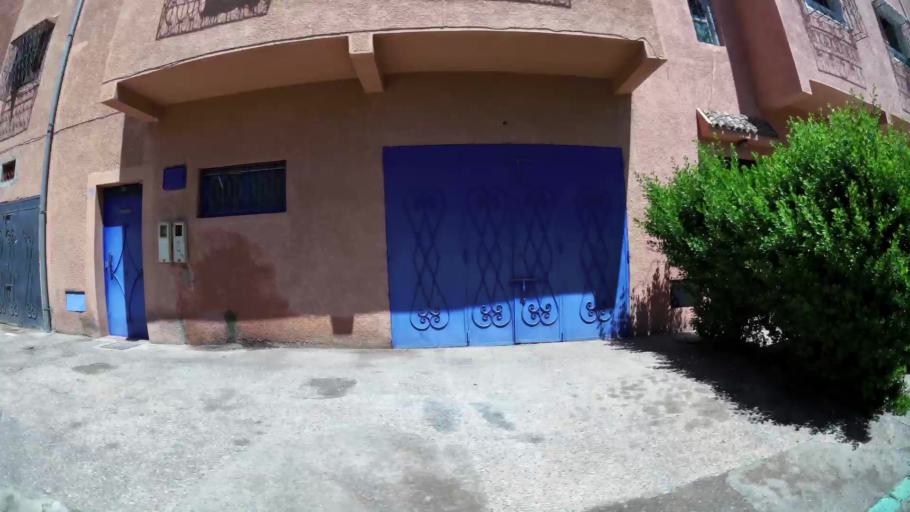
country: MA
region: Marrakech-Tensift-Al Haouz
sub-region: Marrakech
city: Marrakesh
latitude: 31.6380
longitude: -8.0468
